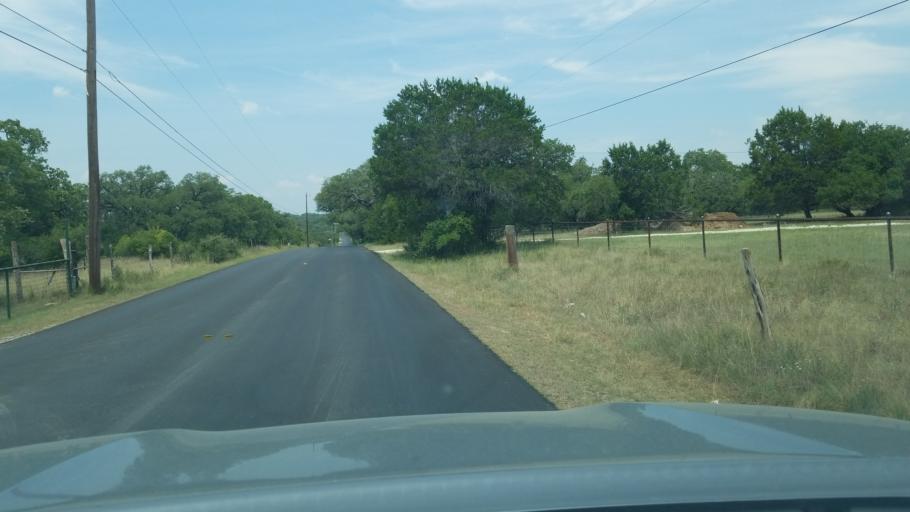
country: US
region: Texas
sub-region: Comal County
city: Bulverde
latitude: 29.7597
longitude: -98.4720
